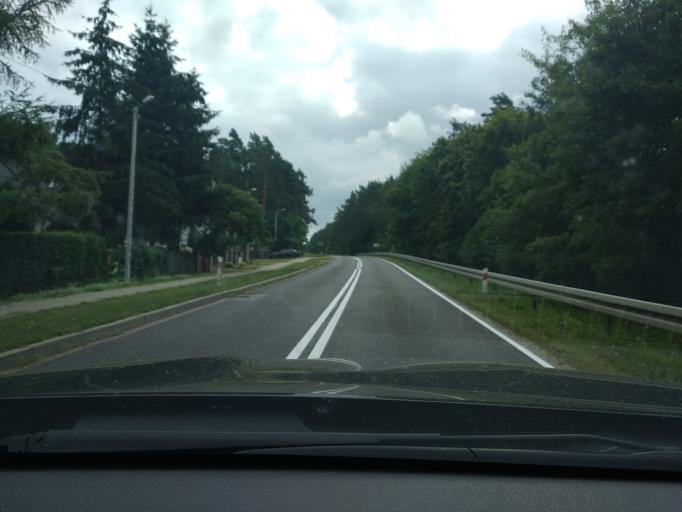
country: PL
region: Masovian Voivodeship
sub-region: Powiat pultuski
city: Obryte
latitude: 52.6462
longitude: 21.2550
